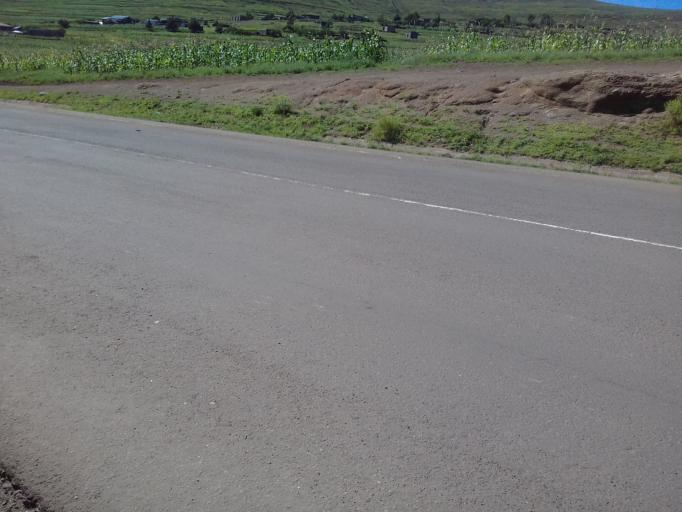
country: LS
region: Thaba-Tseka
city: Thaba-Tseka
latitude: -29.5193
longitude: 28.5828
